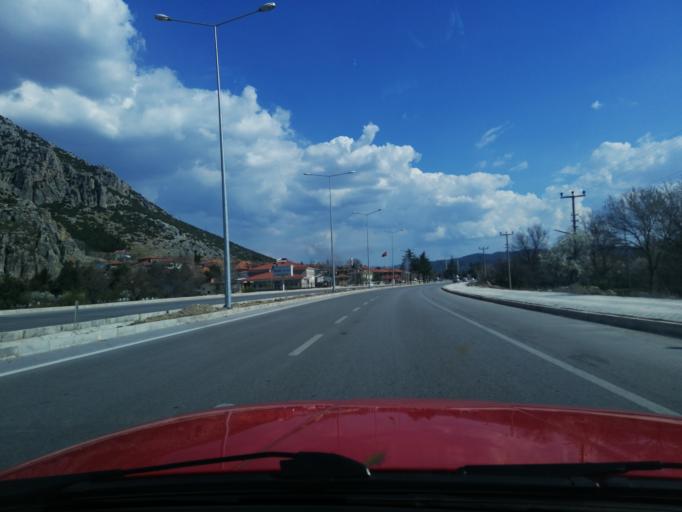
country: TR
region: Burdur
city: Celtikci
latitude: 37.5388
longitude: 30.4771
